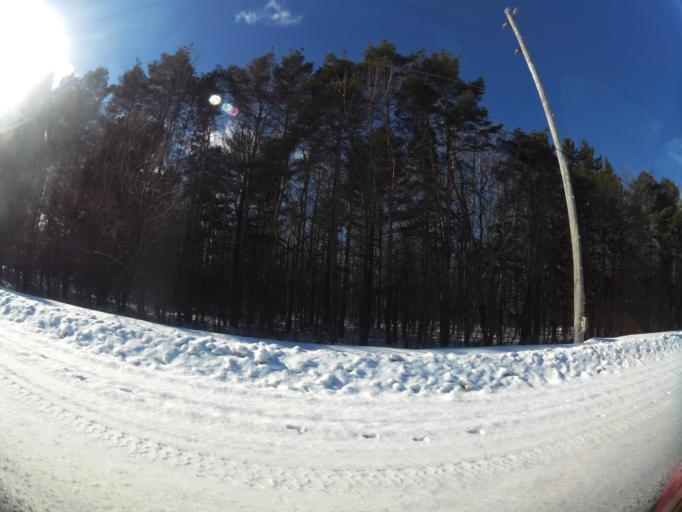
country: CA
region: Ontario
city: Ottawa
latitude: 45.3570
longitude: -75.5600
